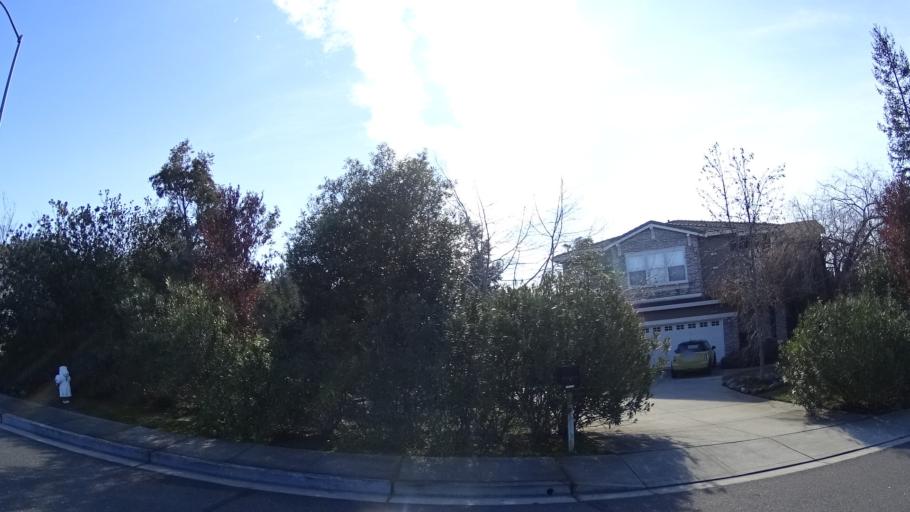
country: US
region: California
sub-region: Alameda County
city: Fairview
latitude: 37.6763
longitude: -122.0381
